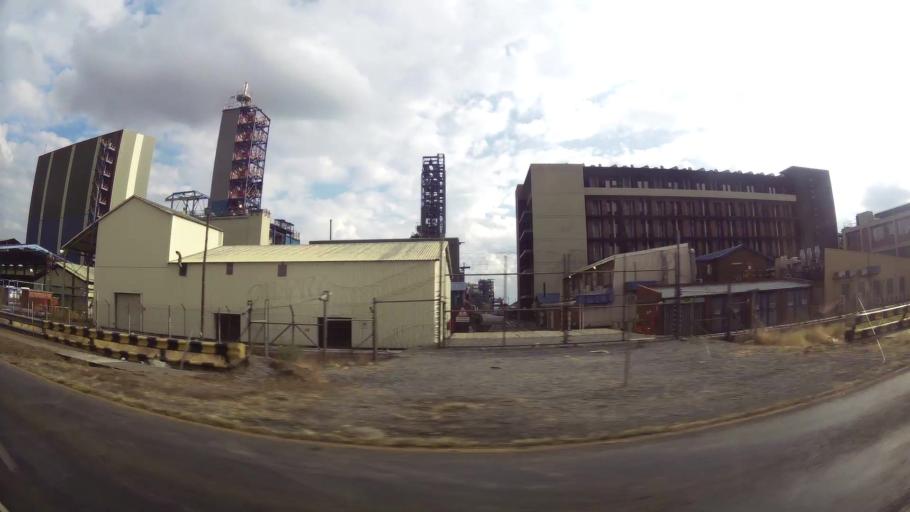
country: ZA
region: Orange Free State
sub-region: Fezile Dabi District Municipality
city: Sasolburg
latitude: -26.8209
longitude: 27.8448
